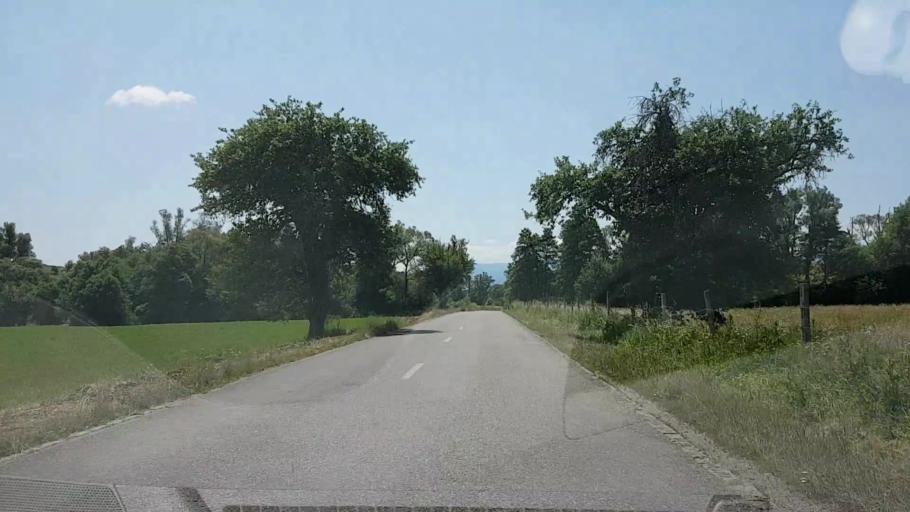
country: RO
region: Brasov
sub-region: Comuna Voila
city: Voila
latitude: 45.8594
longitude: 24.8272
